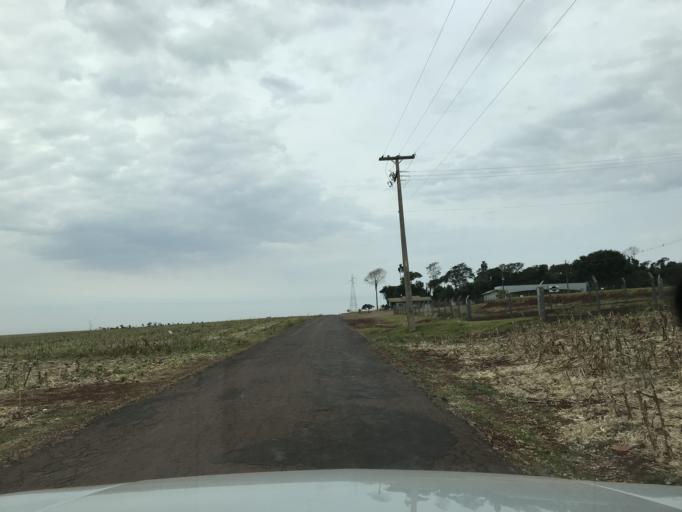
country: BR
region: Parana
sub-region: Palotina
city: Palotina
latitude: -24.2848
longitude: -53.7928
